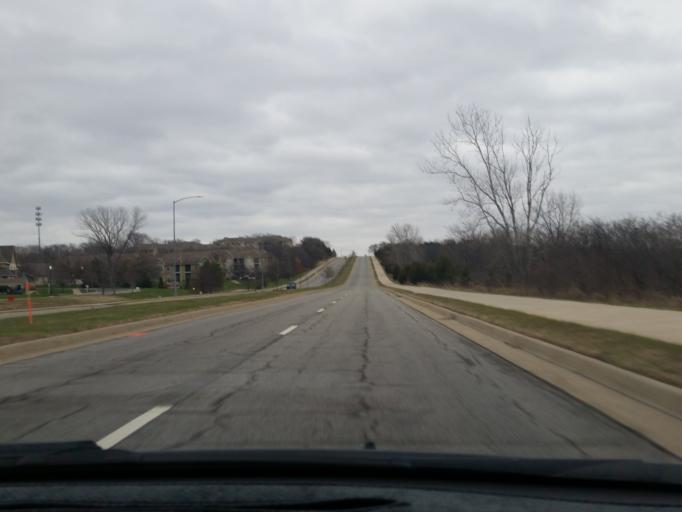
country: US
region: Kansas
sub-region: Douglas County
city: Lawrence
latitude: 38.9425
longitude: -95.3159
